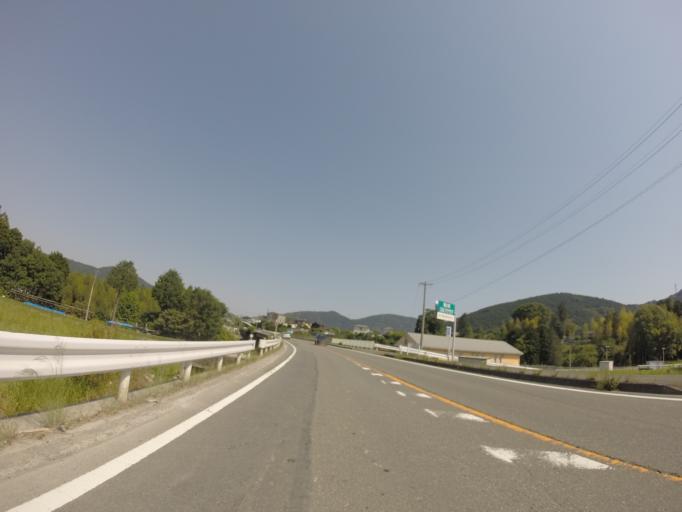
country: JP
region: Shizuoka
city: Fujinomiya
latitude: 35.1895
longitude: 138.5913
